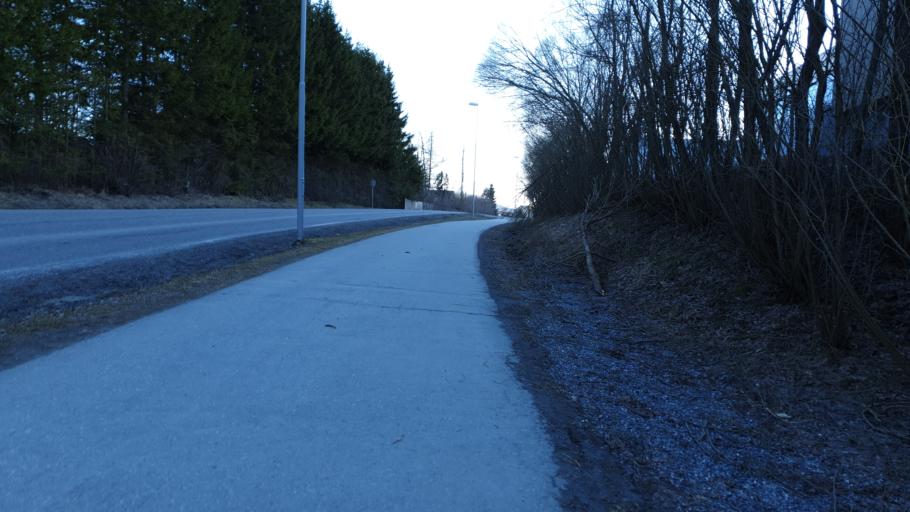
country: NO
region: Sor-Trondelag
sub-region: Orkdal
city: Orkanger
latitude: 63.2918
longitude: 9.8435
